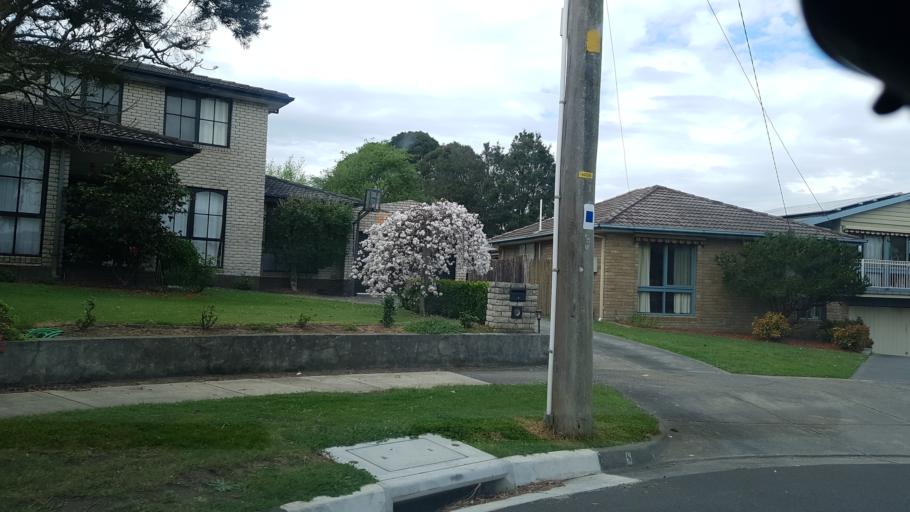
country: AU
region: Victoria
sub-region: Monash
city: Mulgrave
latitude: -37.9148
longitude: 145.1769
